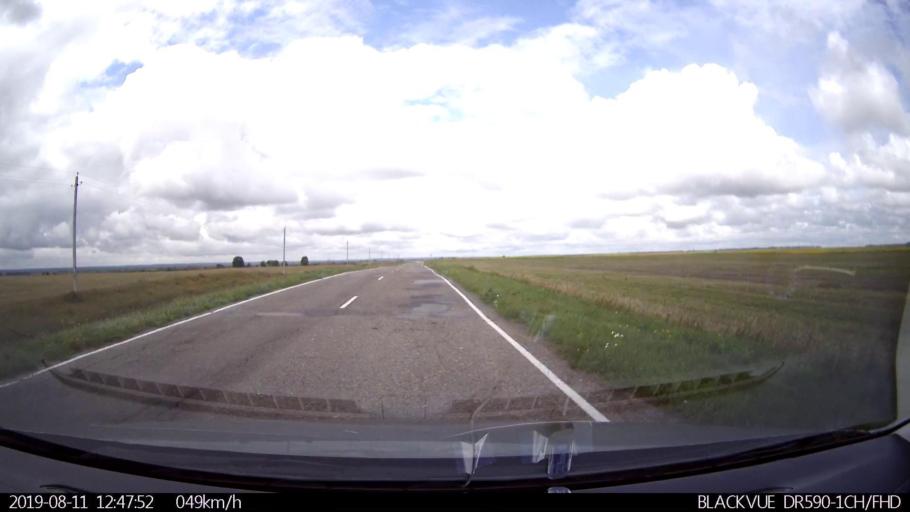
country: RU
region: Ulyanovsk
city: Ignatovka
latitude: 53.8713
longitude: 47.7046
